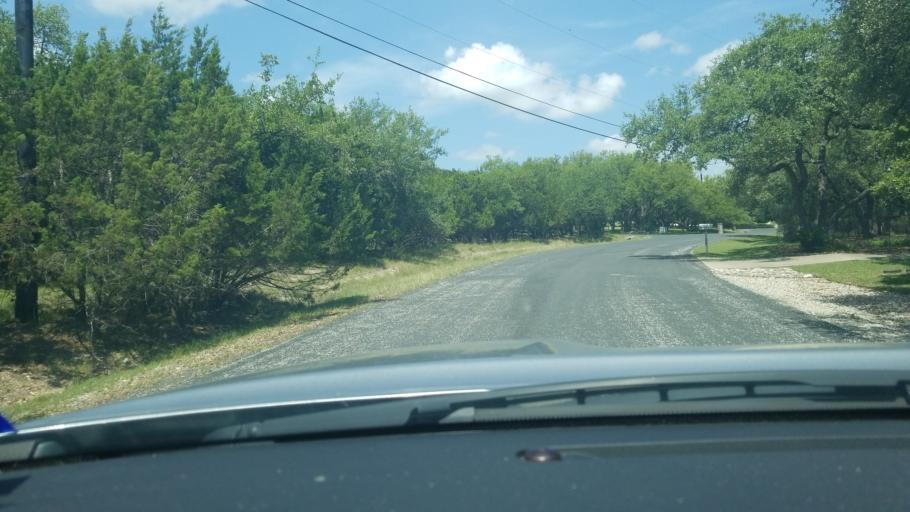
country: US
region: Texas
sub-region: Bexar County
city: Timberwood Park
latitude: 29.6893
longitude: -98.4811
